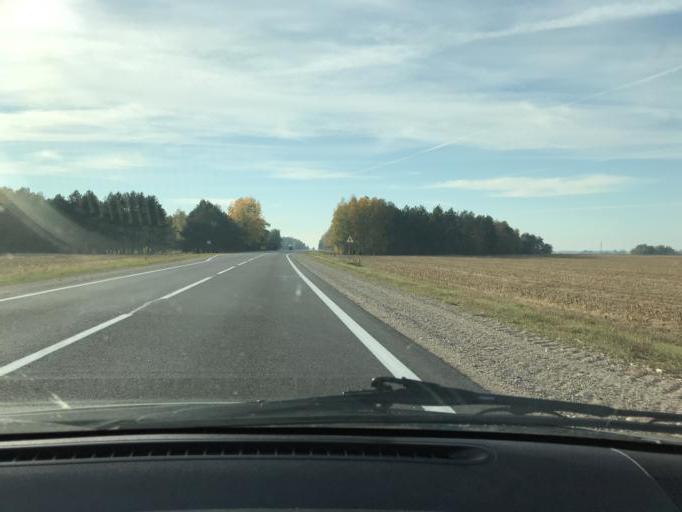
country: BY
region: Brest
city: Horad Pinsk
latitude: 52.1477
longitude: 25.9002
